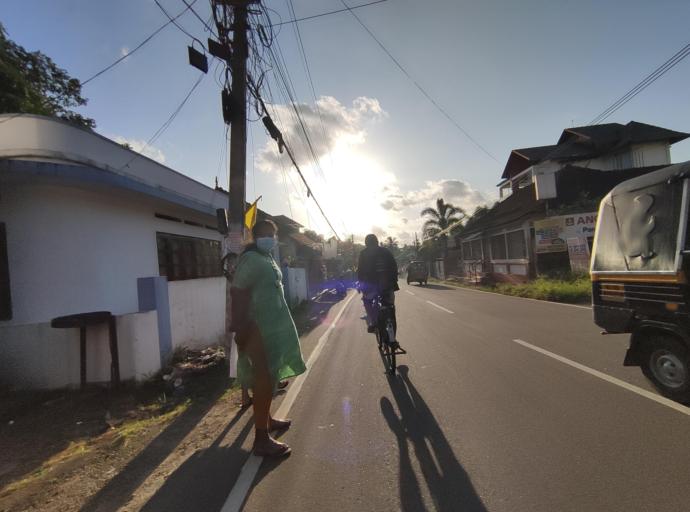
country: IN
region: Kerala
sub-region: Kottayam
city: Kottayam
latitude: 9.5833
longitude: 76.5079
